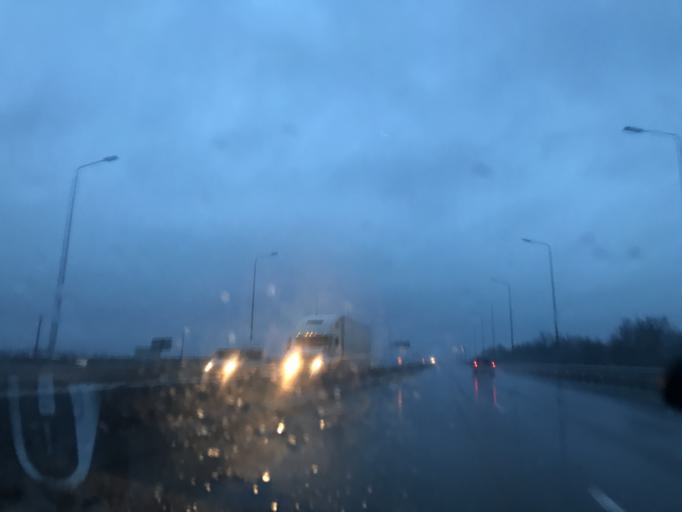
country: RU
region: Rostov
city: Samarskoye
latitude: 47.0040
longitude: 39.7312
